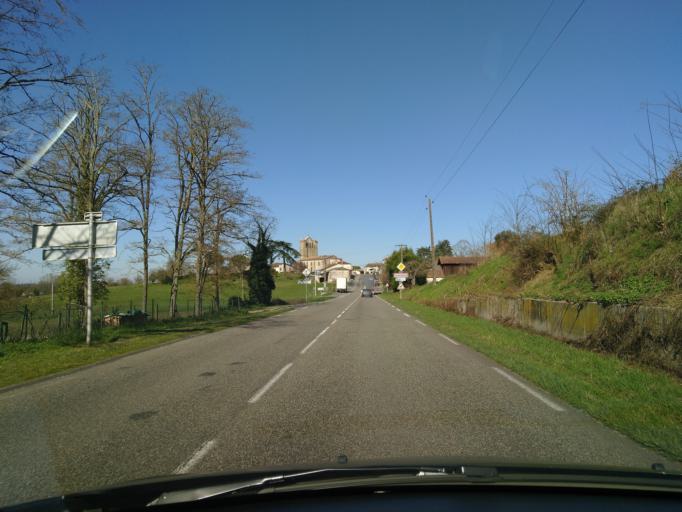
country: FR
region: Aquitaine
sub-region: Departement du Lot-et-Garonne
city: Cancon
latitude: 44.5805
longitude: 0.6241
